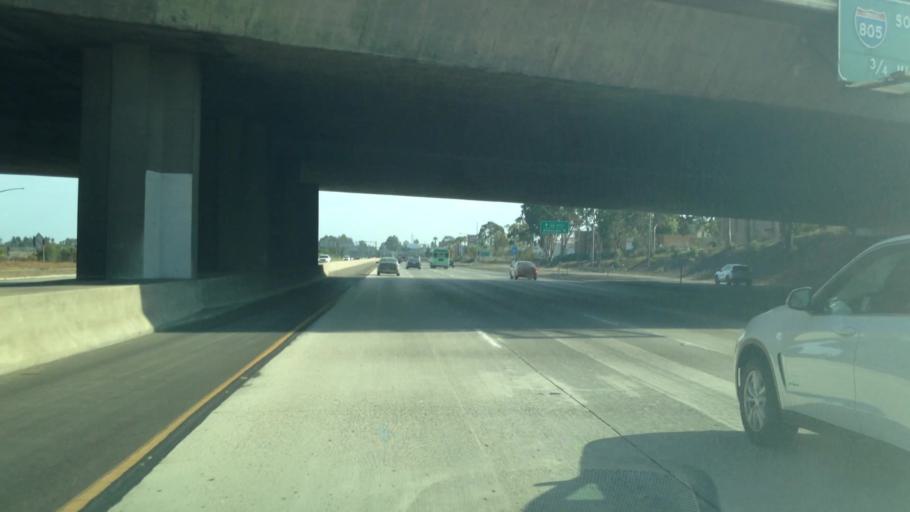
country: US
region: California
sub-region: San Diego County
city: San Diego
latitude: 32.8222
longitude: -117.1465
